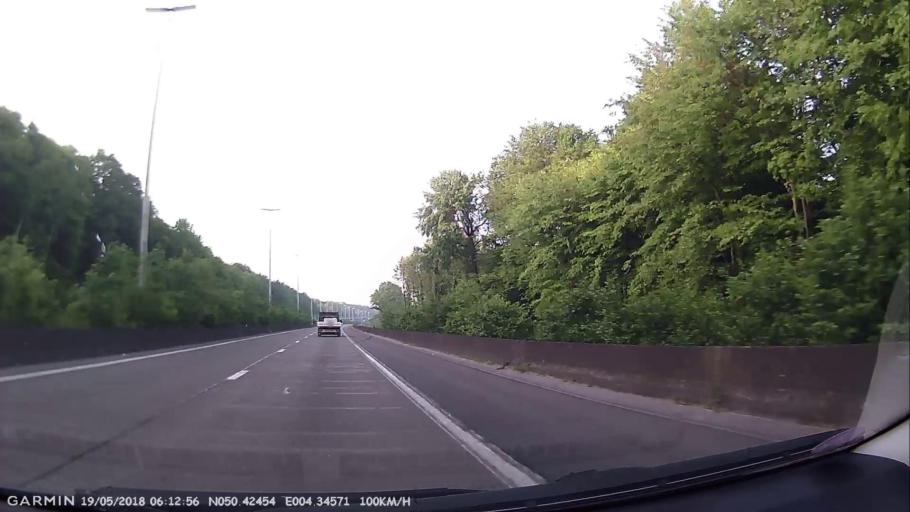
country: BE
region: Wallonia
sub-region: Province du Hainaut
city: Courcelles
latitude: 50.4242
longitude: 4.3458
